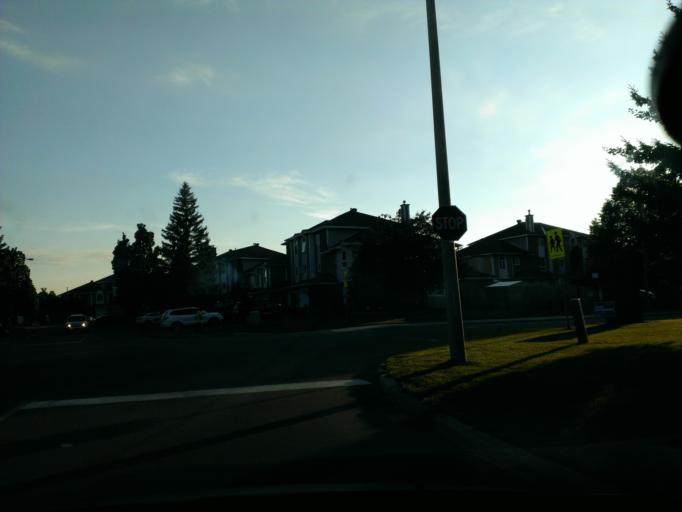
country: CA
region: Quebec
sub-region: Outaouais
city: Gatineau
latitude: 45.4789
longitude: -75.4941
